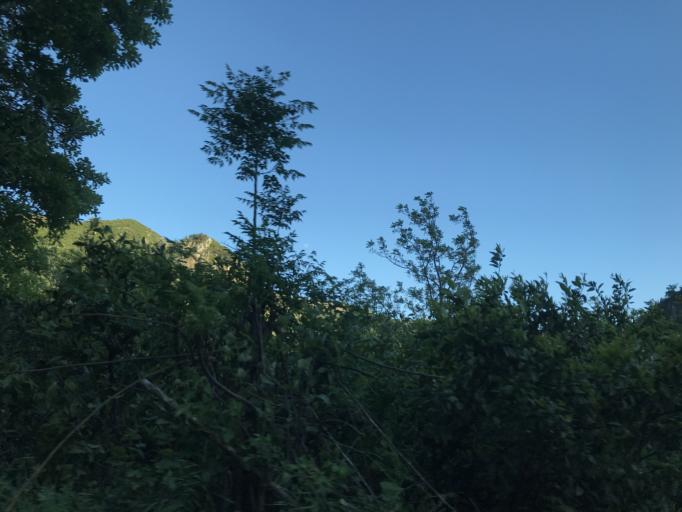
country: TR
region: Hatay
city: Samandag
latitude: 36.0764
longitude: 36.0328
